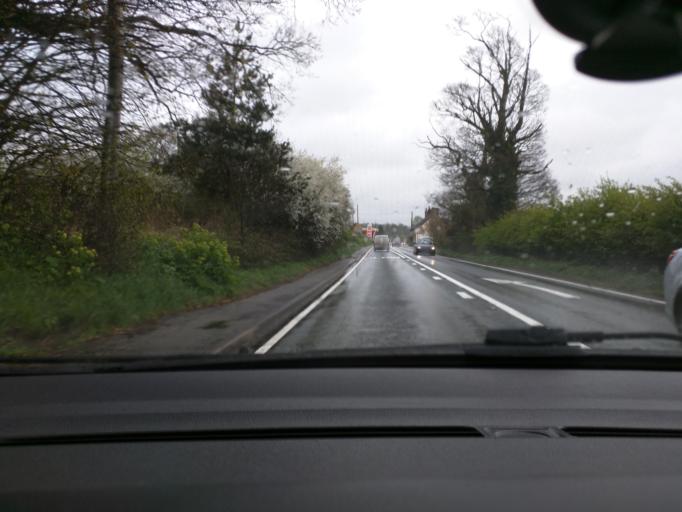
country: GB
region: England
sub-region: Suffolk
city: Saxmundham
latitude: 52.1870
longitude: 1.4461
